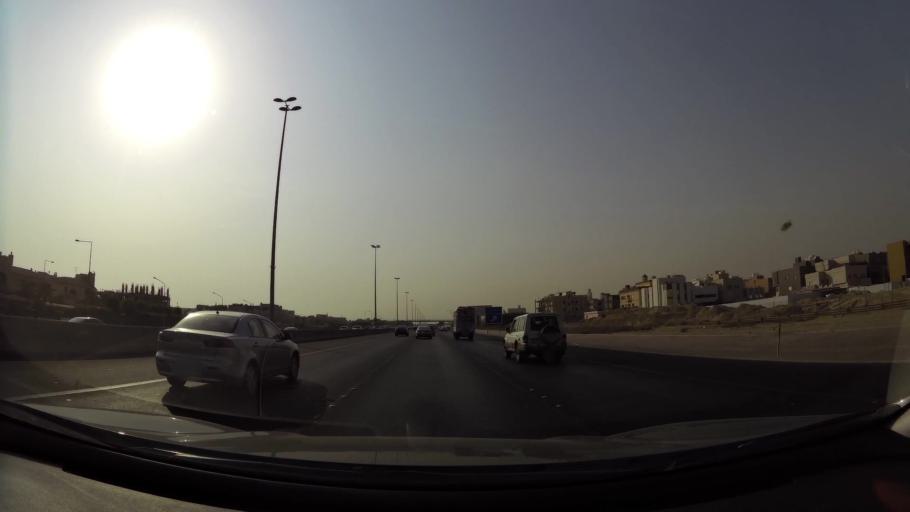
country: KW
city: Al Funaytis
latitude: 29.2383
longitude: 48.0952
